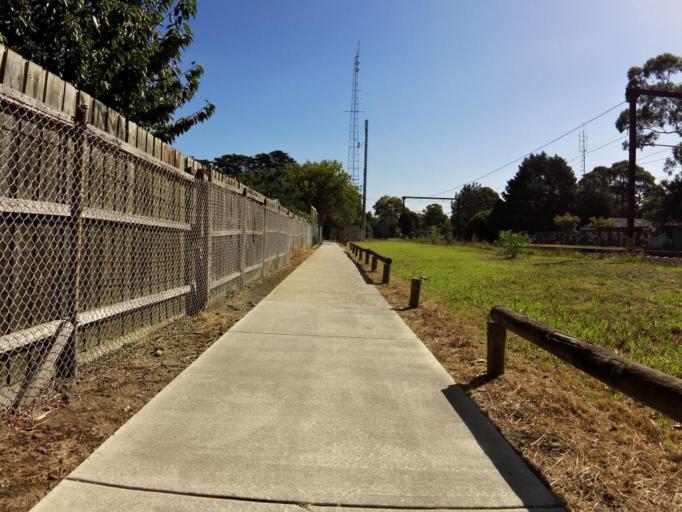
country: AU
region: Victoria
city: Burwood East
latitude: -37.8754
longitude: 145.1396
